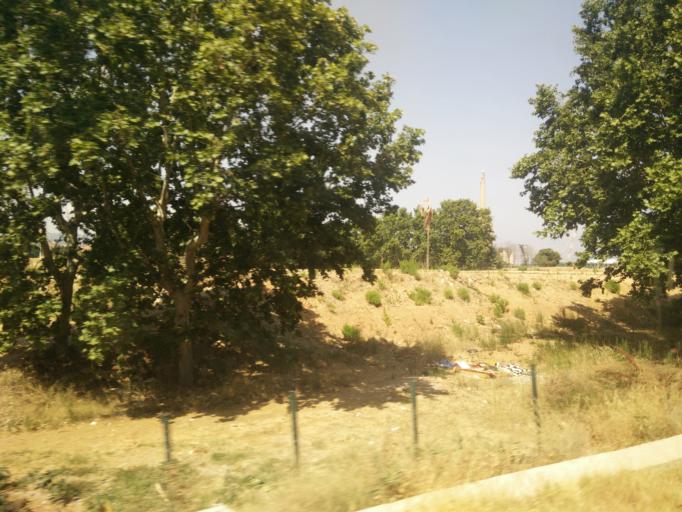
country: ES
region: Catalonia
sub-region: Provincia de Barcelona
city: Sant Adria de Besos
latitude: 41.4200
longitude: 2.2244
